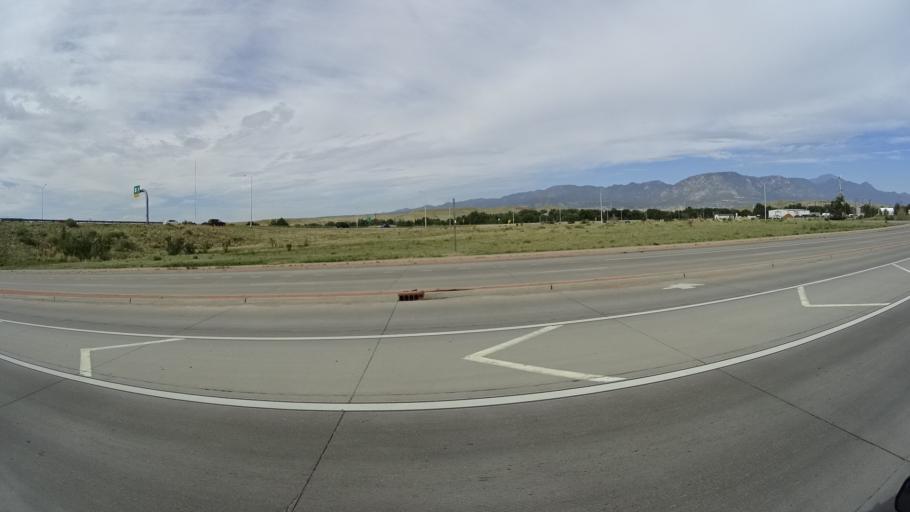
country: US
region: Colorado
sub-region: El Paso County
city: Security-Widefield
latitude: 38.7239
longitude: -104.7190
